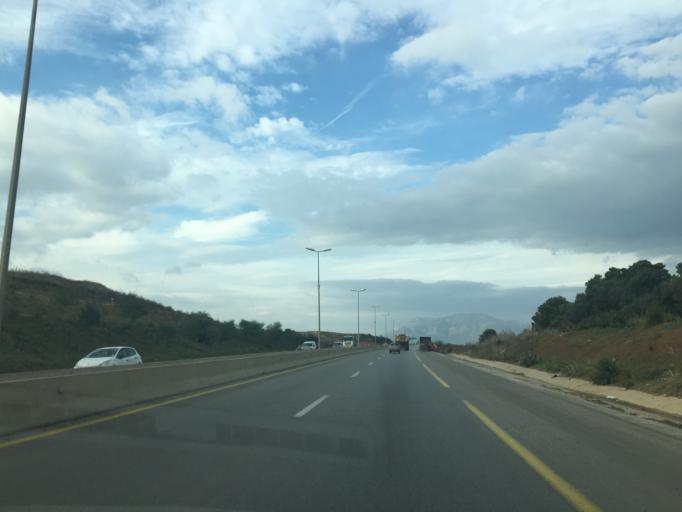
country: DZ
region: Tipaza
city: Tipasa
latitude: 36.5753
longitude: 2.5187
